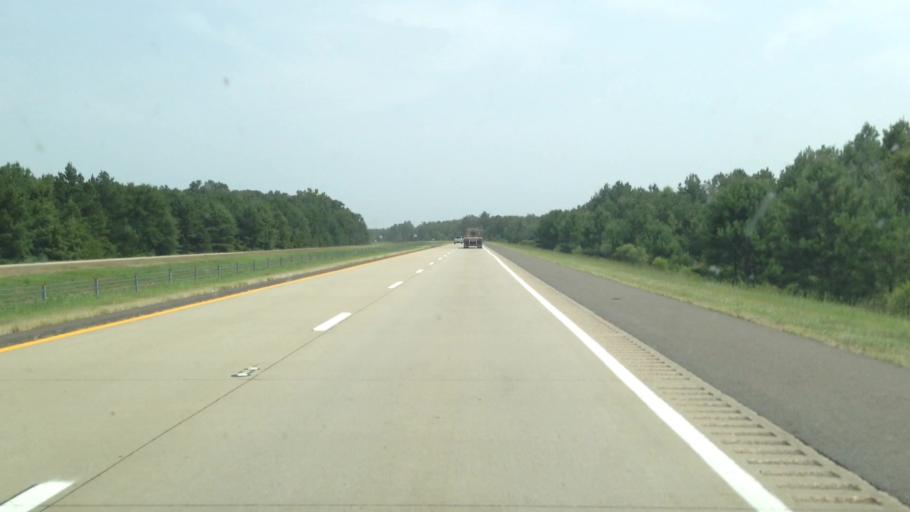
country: US
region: Texas
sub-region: Bowie County
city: Texarkana
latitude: 33.2065
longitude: -93.8755
